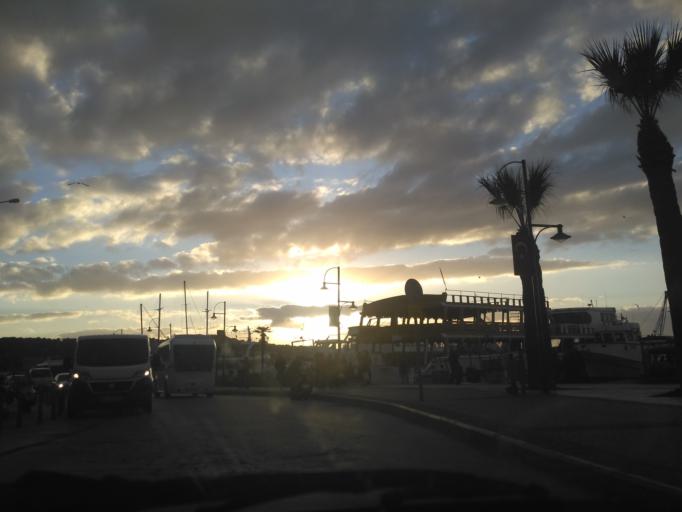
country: TR
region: Balikesir
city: Ayvalik
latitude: 39.3178
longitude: 26.6917
